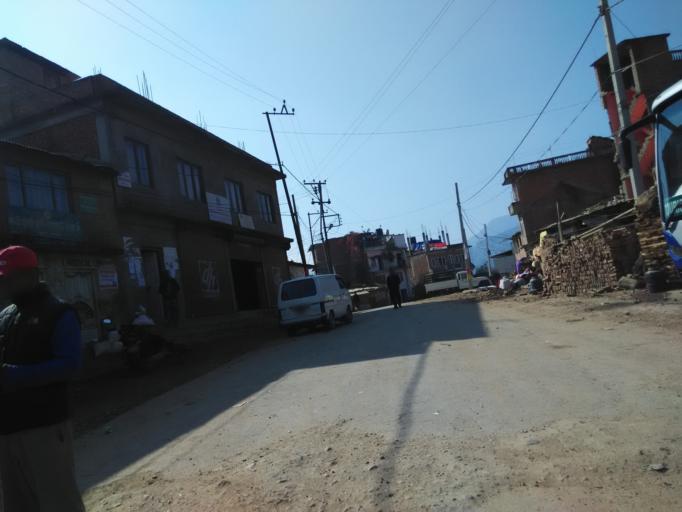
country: NP
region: Central Region
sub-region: Bagmati Zone
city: Patan
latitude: 27.6282
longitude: 85.3033
